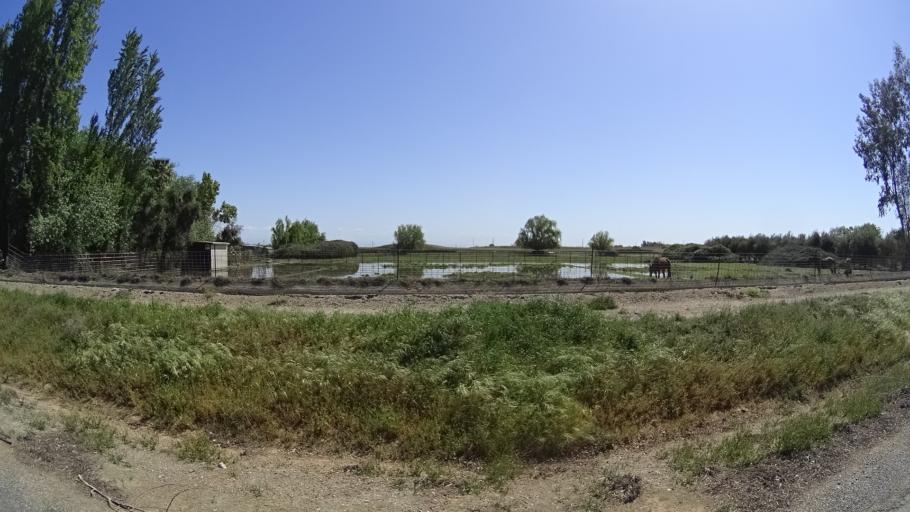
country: US
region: California
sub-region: Glenn County
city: Orland
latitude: 39.7718
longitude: -122.1597
